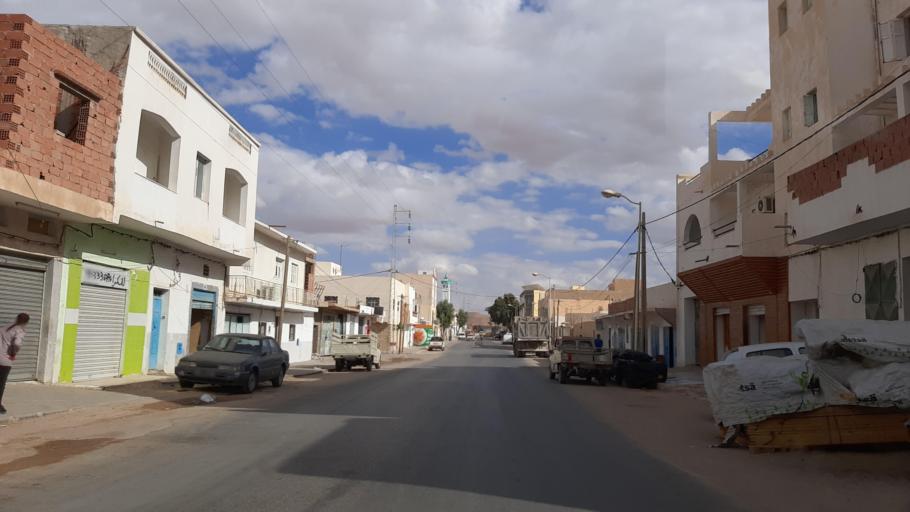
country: TN
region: Tataouine
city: Tataouine
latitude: 32.9212
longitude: 10.4627
